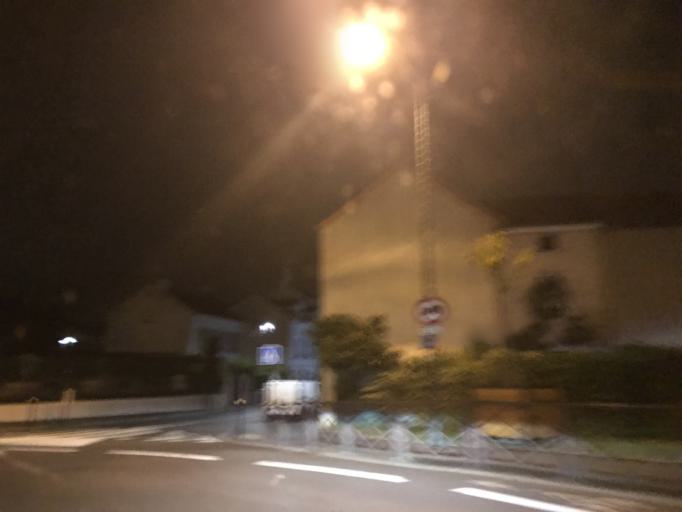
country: FR
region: Ile-de-France
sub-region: Departement des Yvelines
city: Maisons-Laffitte
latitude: 48.9423
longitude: 2.1632
